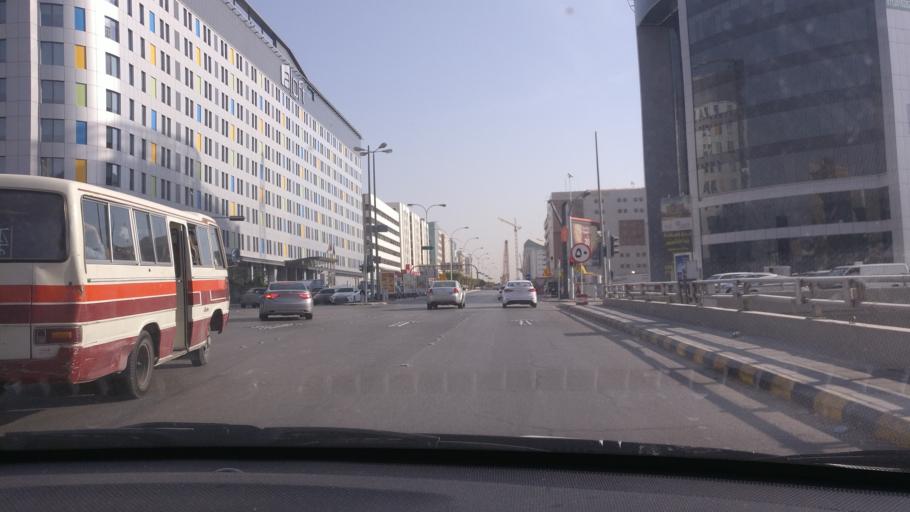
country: SA
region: Ar Riyad
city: Riyadh
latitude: 24.6803
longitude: 46.6919
